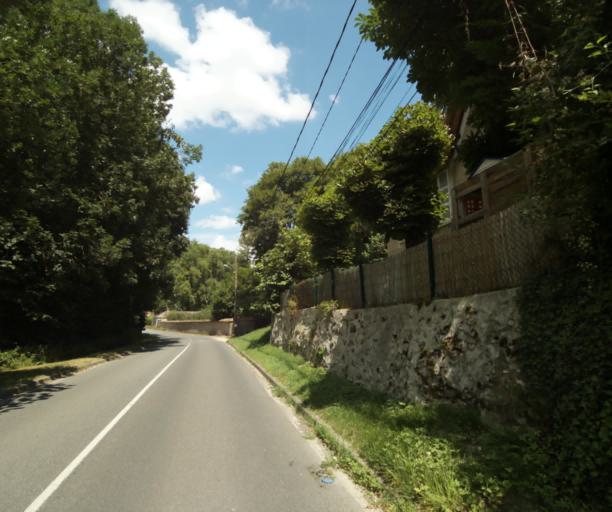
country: FR
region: Ile-de-France
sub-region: Departement de Seine-et-Marne
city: Hericy
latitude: 48.4611
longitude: 2.7726
